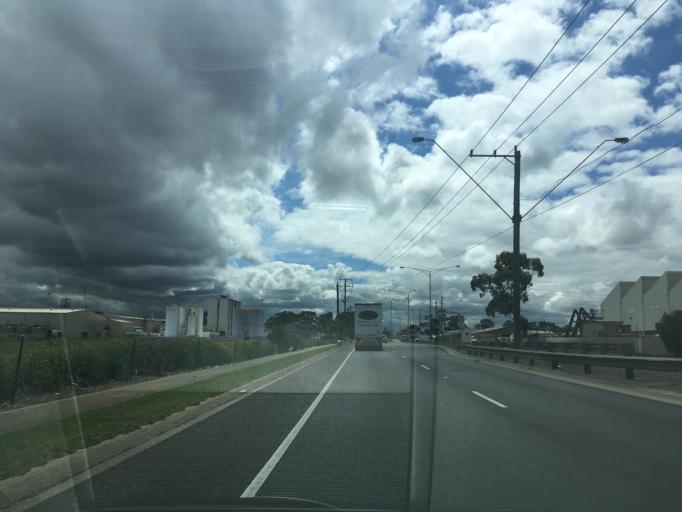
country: AU
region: Victoria
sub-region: Hobsons Bay
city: Laverton
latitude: -37.8391
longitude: 144.7830
